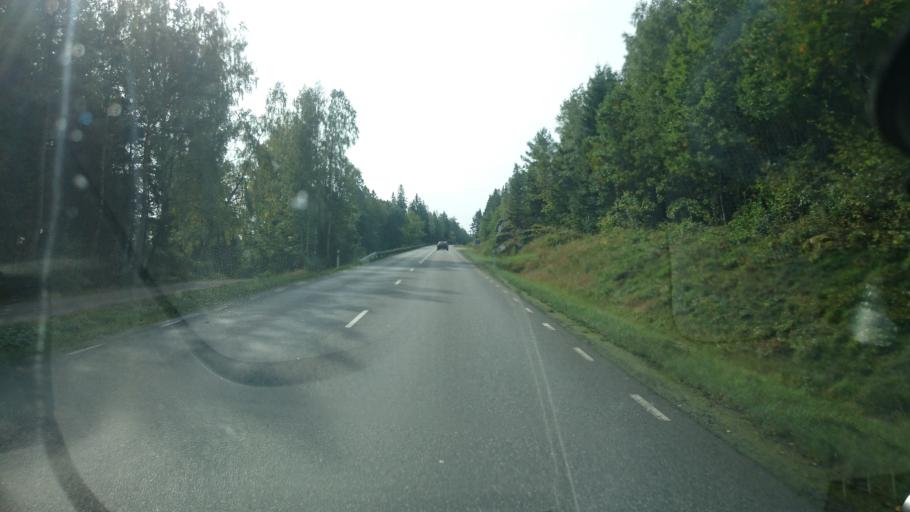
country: SE
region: Vaestra Goetaland
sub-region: Alingsas Kommun
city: Sollebrunn
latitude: 58.0389
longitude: 12.4662
